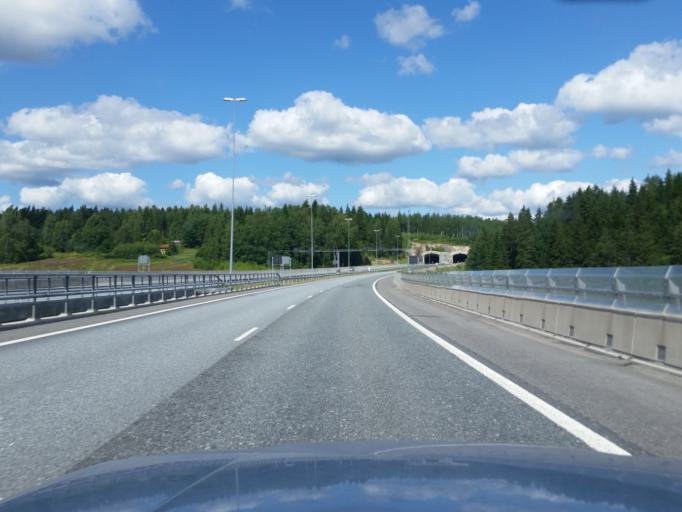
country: FI
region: Uusimaa
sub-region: Helsinki
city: Saukkola
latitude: 60.3300
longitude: 23.9337
